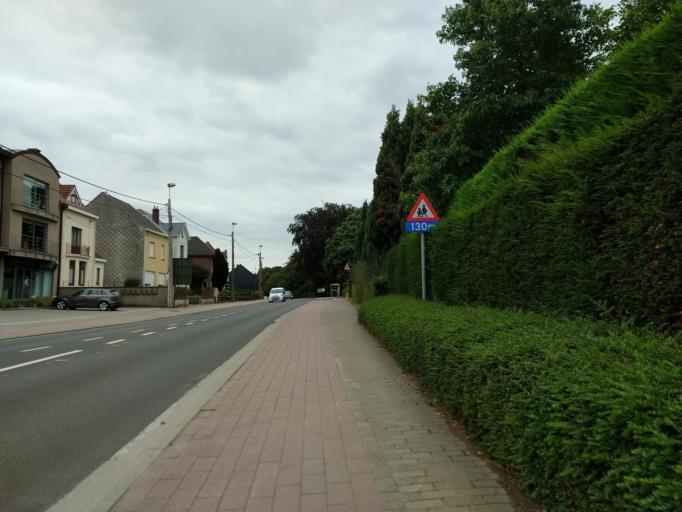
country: BE
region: Flanders
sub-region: Provincie Vlaams-Brabant
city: Overijse
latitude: 50.7781
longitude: 4.5219
